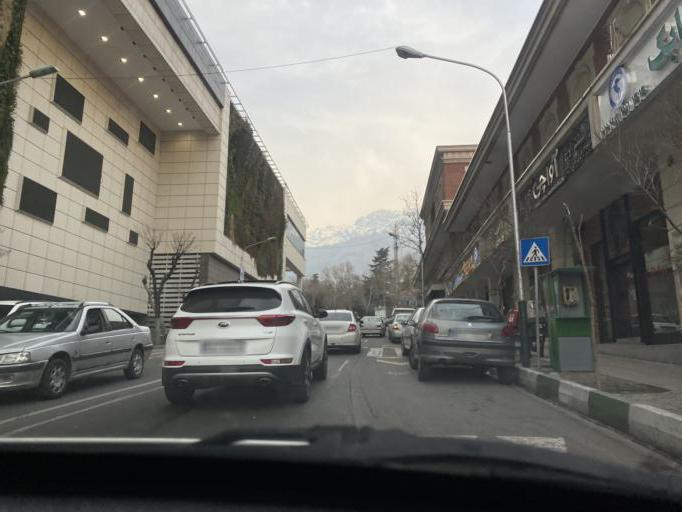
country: IR
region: Tehran
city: Tajrish
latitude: 35.8058
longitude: 51.4723
